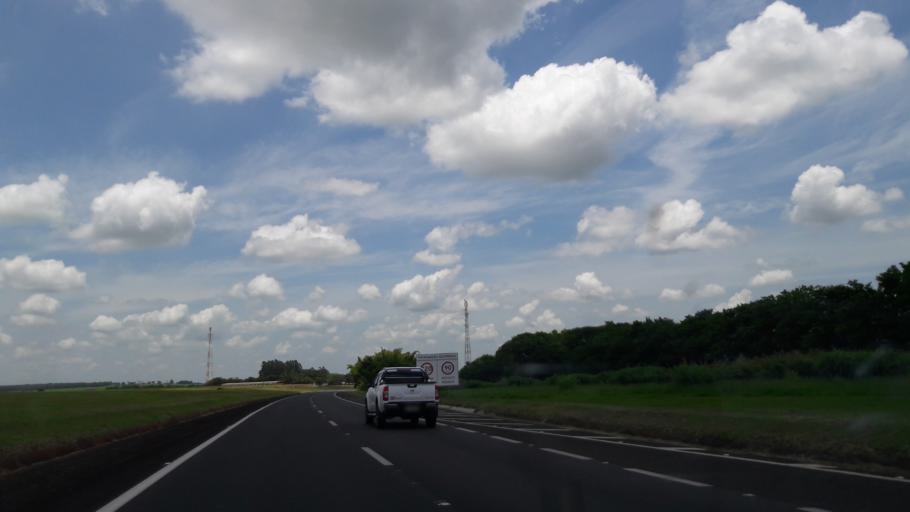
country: BR
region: Sao Paulo
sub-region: Avare
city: Avare
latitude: -22.9573
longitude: -48.8549
